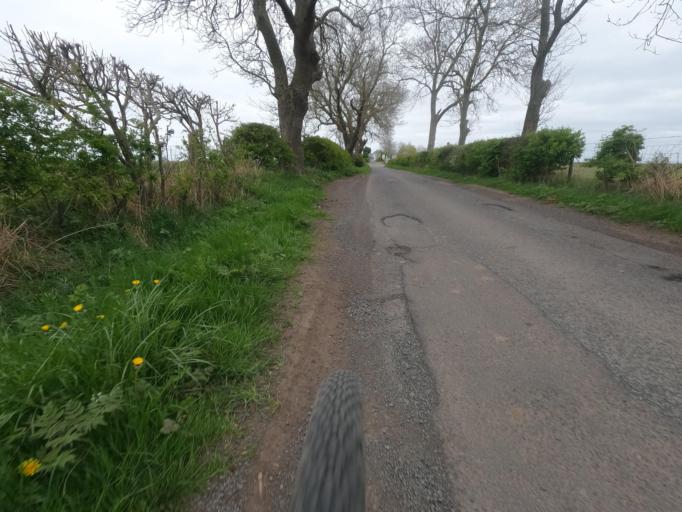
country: GB
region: England
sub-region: Northumberland
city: Darras Hall
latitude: 55.0776
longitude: -1.7866
